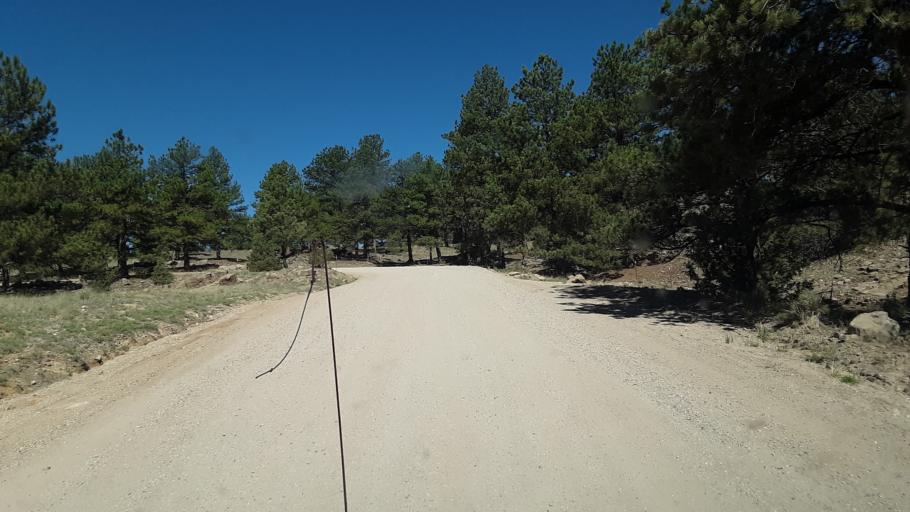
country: US
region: Colorado
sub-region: Custer County
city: Westcliffe
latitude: 38.2125
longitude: -105.4428
